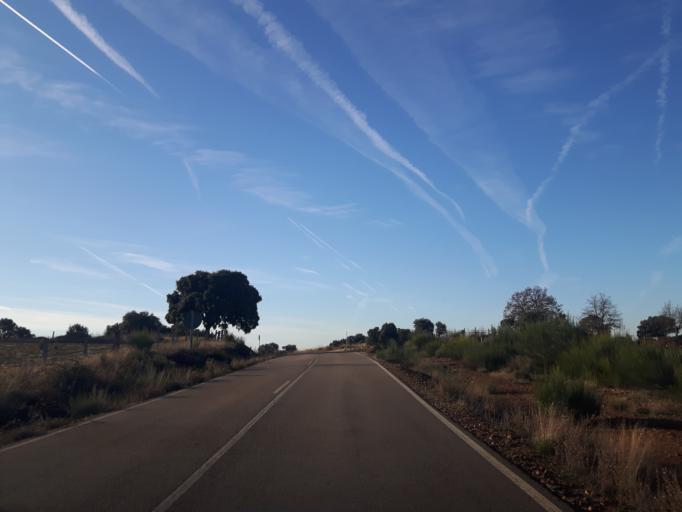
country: ES
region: Castille and Leon
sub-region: Provincia de Salamanca
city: Olmedo de Camaces
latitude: 40.8987
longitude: -6.6225
